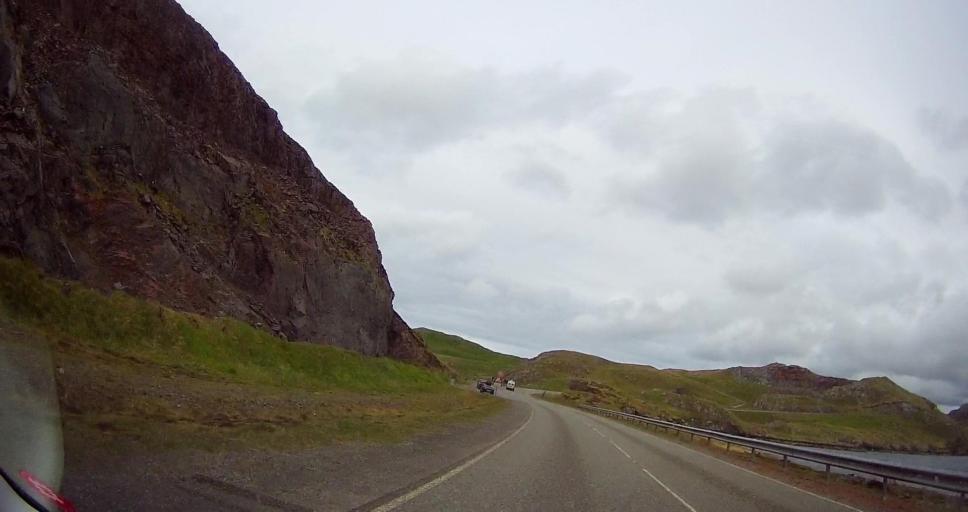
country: GB
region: Scotland
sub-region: Shetland Islands
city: Lerwick
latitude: 60.3965
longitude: -1.3813
